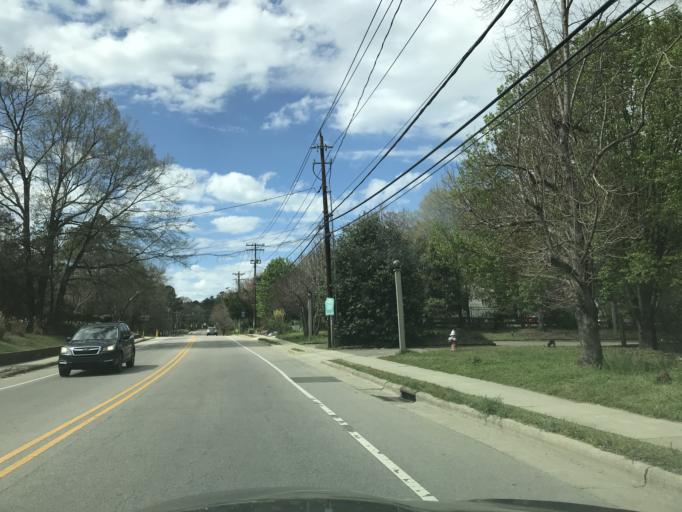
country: US
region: North Carolina
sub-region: Orange County
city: Carrboro
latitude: 35.9165
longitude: -79.0729
